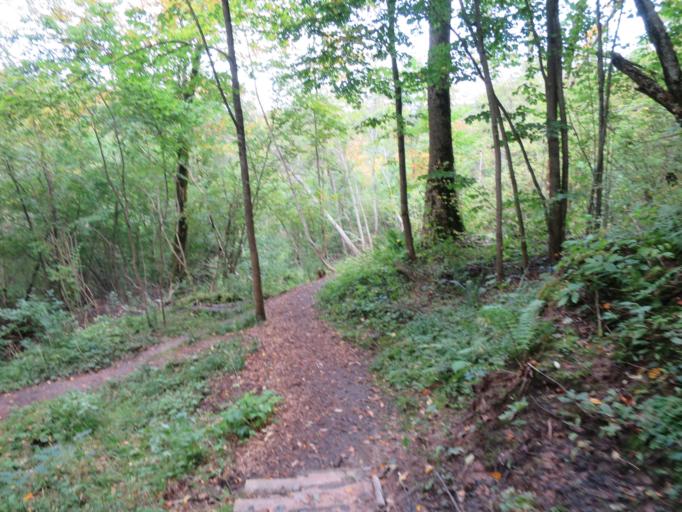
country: LV
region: Sigulda
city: Sigulda
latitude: 57.1709
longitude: 24.8308
